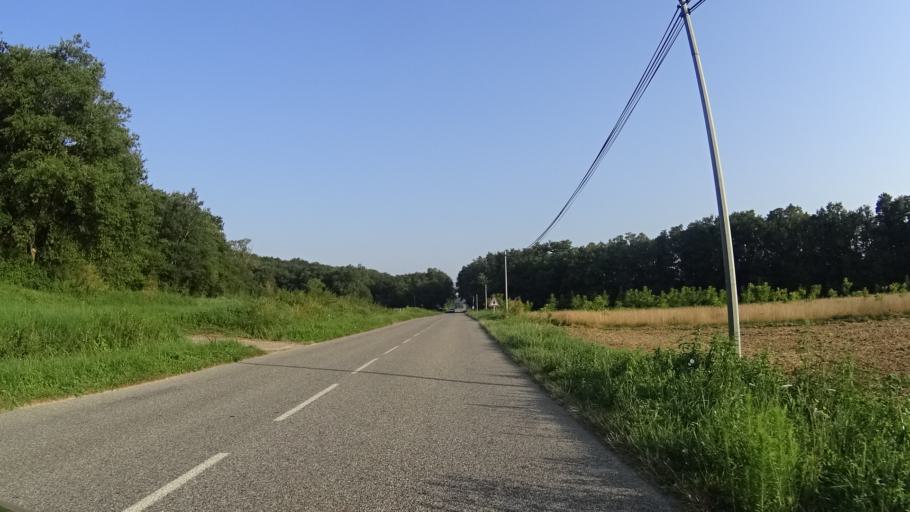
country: FR
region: Midi-Pyrenees
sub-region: Departement de l'Ariege
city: Mirepoix
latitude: 43.0753
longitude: 1.9395
